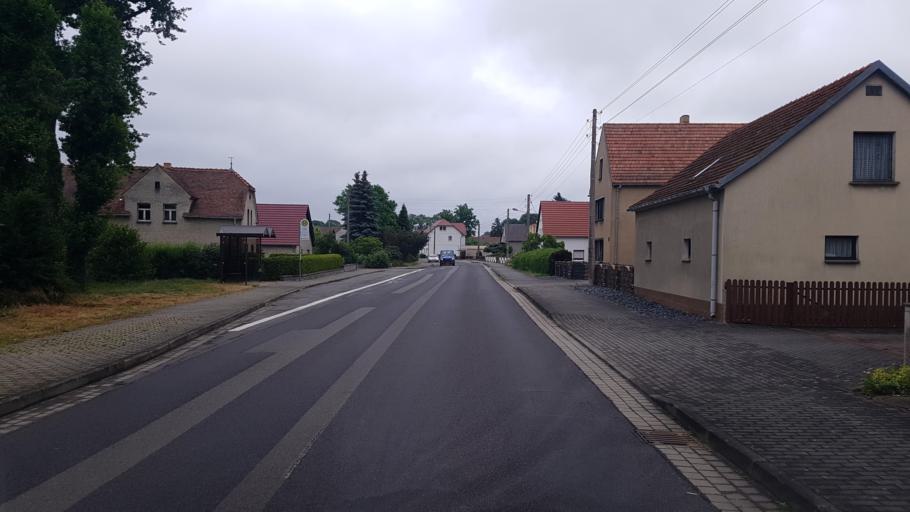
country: DE
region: Brandenburg
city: Kroppen
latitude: 51.3846
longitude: 13.8009
